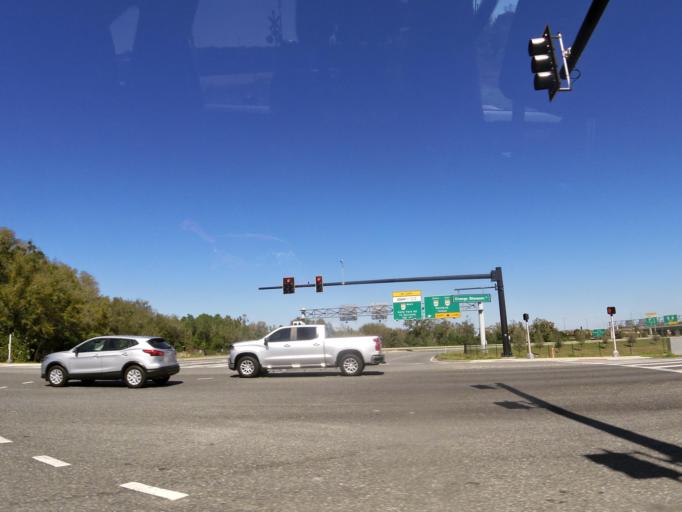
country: US
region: Florida
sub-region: Orange County
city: Zellwood
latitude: 28.6964
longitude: -81.5628
